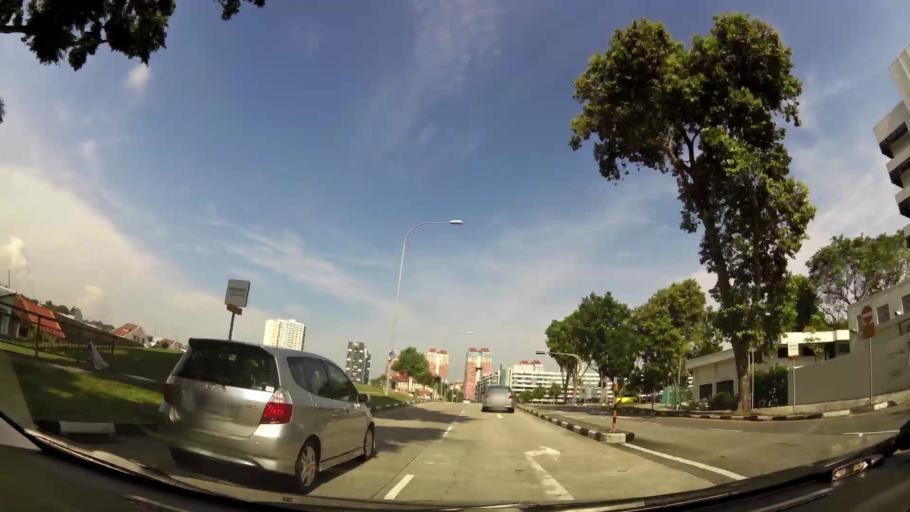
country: SG
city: Singapore
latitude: 1.3559
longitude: 103.8365
